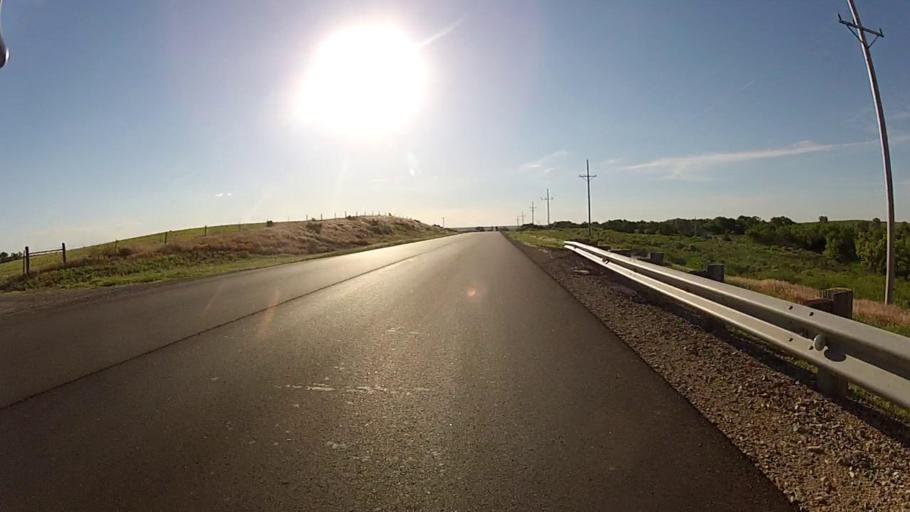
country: US
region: Kansas
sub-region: Comanche County
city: Coldwater
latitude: 37.2820
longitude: -99.0876
